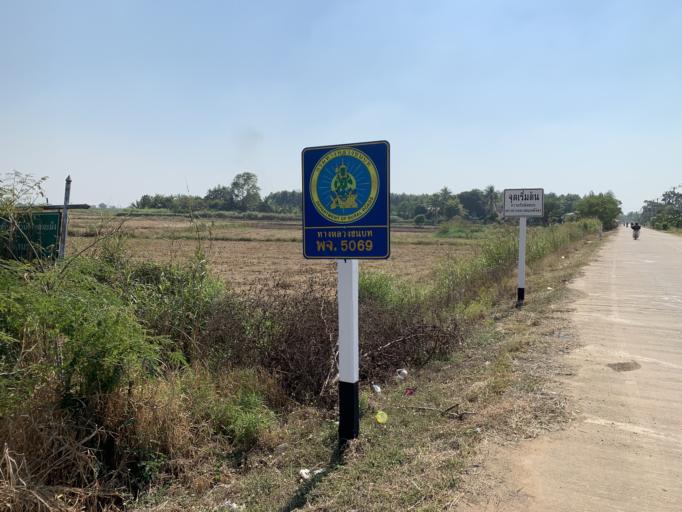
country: TH
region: Phichit
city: Phichit
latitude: 16.3910
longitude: 100.3904
